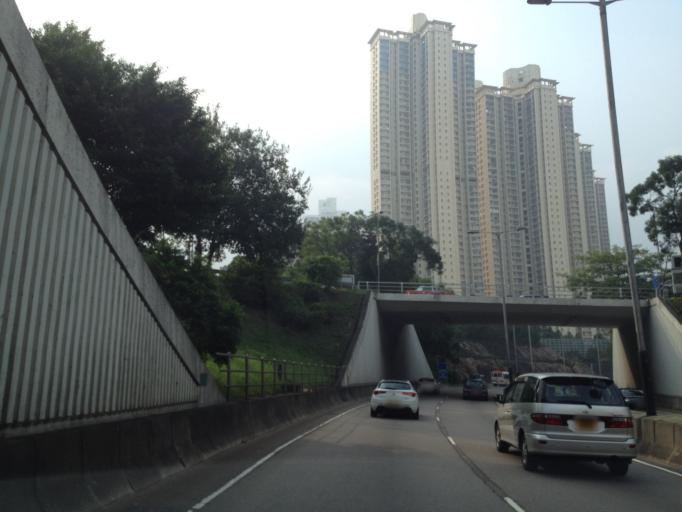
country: HK
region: Kowloon City
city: Kowloon
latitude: 22.3048
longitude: 114.2350
